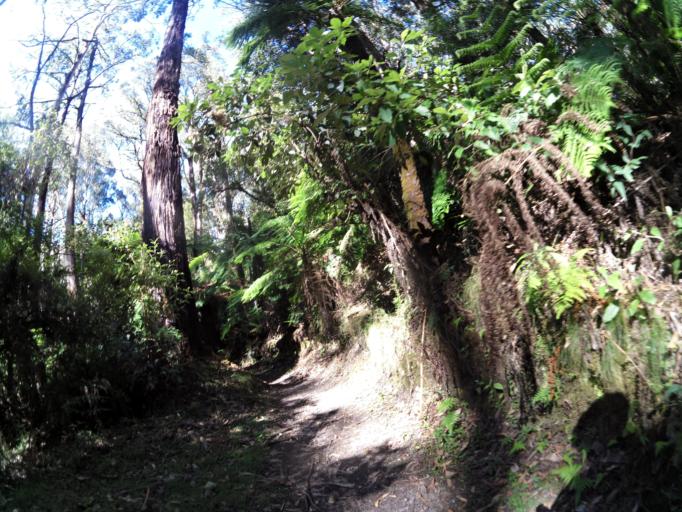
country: AU
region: Victoria
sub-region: Colac-Otway
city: Apollo Bay
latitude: -38.5503
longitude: 143.7395
